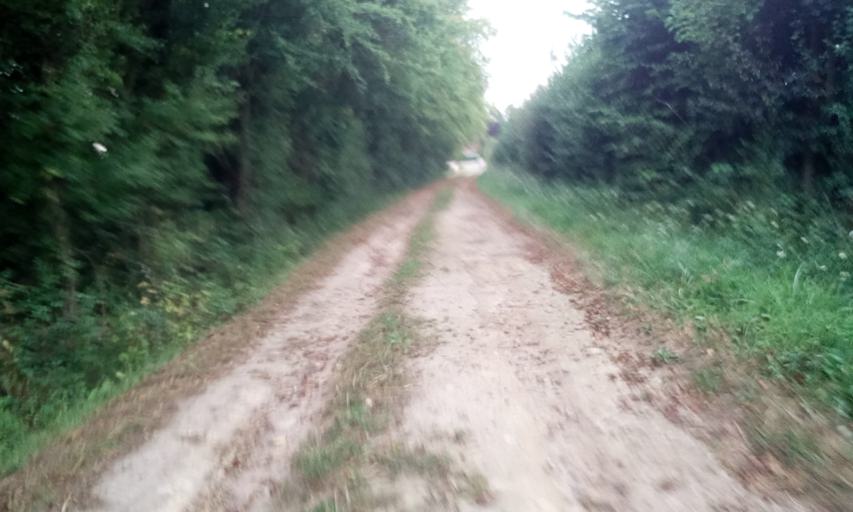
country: FR
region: Lower Normandy
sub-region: Departement du Calvados
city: Sannerville
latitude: 49.1855
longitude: -0.2103
